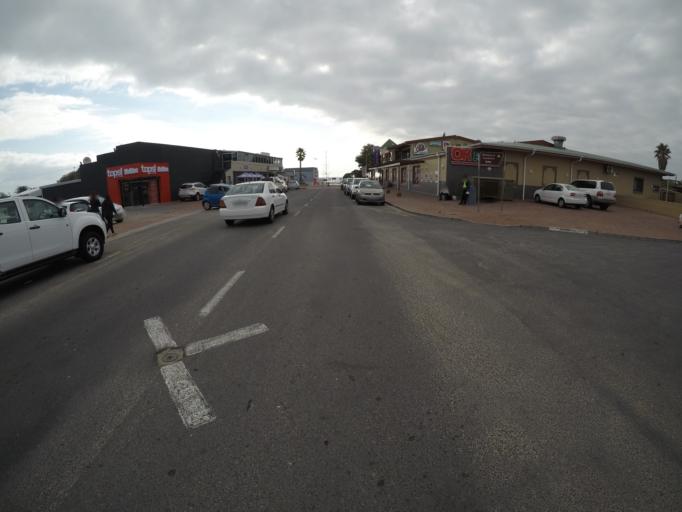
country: ZA
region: Western Cape
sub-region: City of Cape Town
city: Sunset Beach
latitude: -33.7297
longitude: 18.4398
